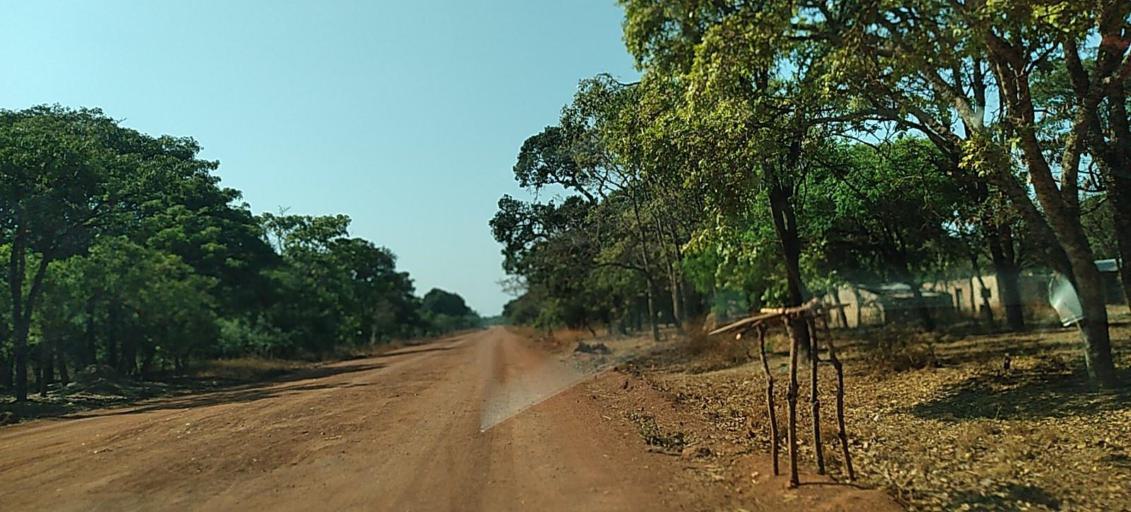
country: ZM
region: North-Western
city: Mwinilunga
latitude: -11.9239
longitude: 25.3194
